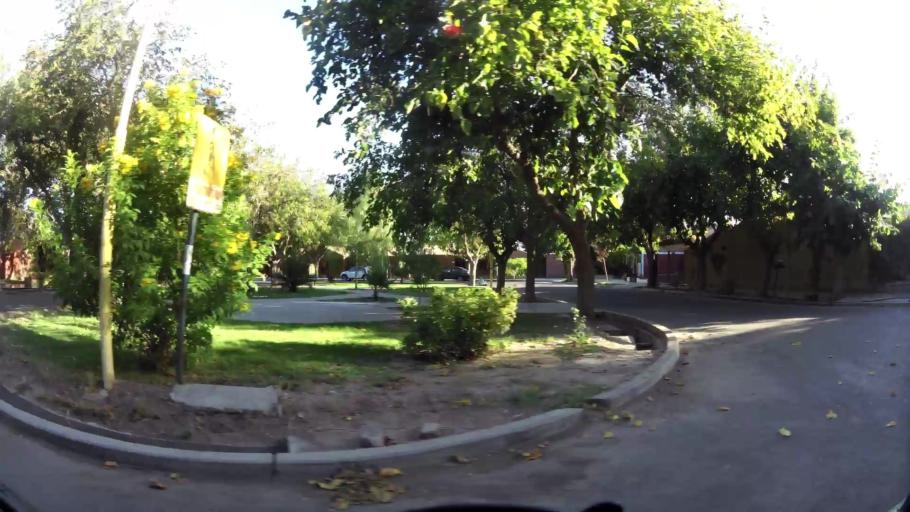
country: AR
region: San Juan
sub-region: Departamento de Santa Lucia
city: Santa Lucia
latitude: -31.5486
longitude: -68.5121
